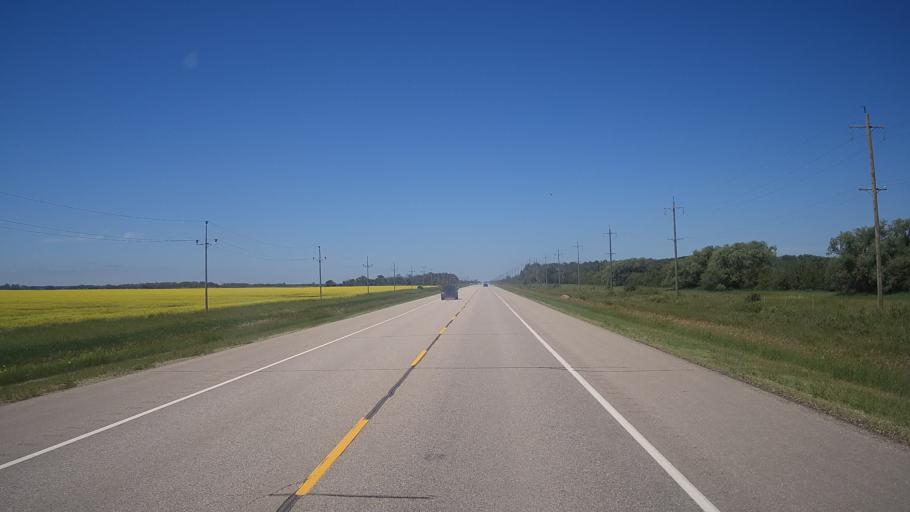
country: CA
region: Manitoba
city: Neepawa
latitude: 50.2257
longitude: -99.0894
